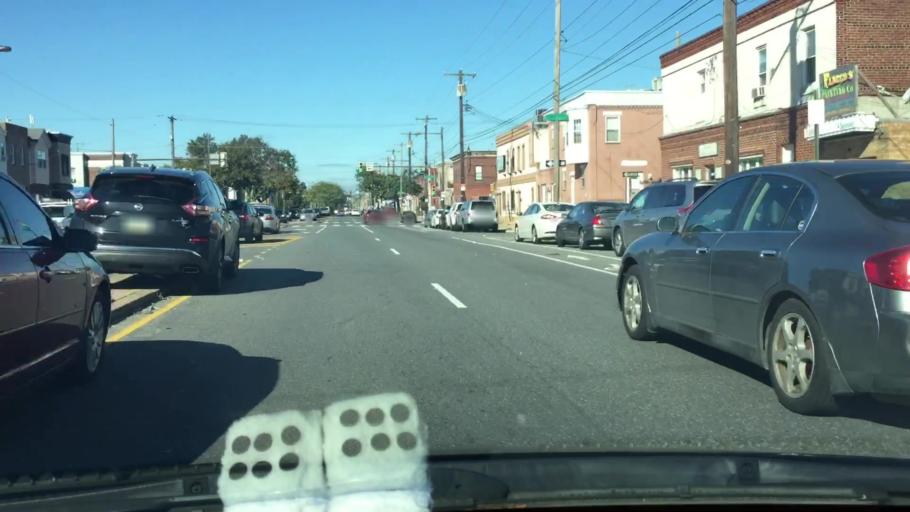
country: US
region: Pennsylvania
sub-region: Philadelphia County
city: Philadelphia
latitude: 39.9174
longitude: -75.1751
